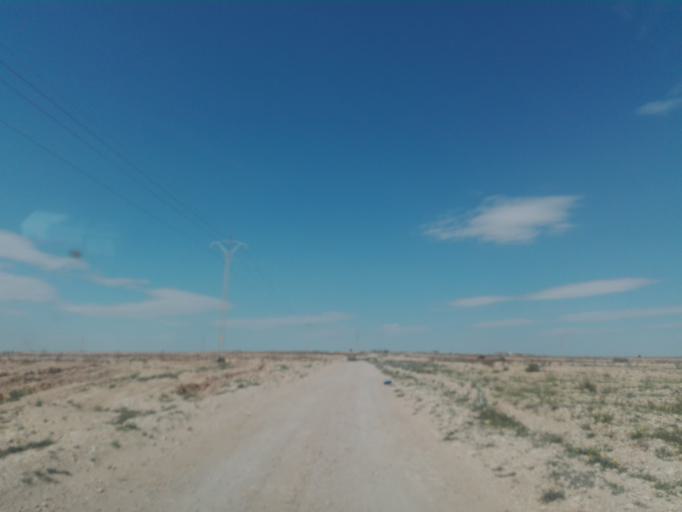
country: TN
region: Safaqis
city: Sfax
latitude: 34.6872
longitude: 10.5464
